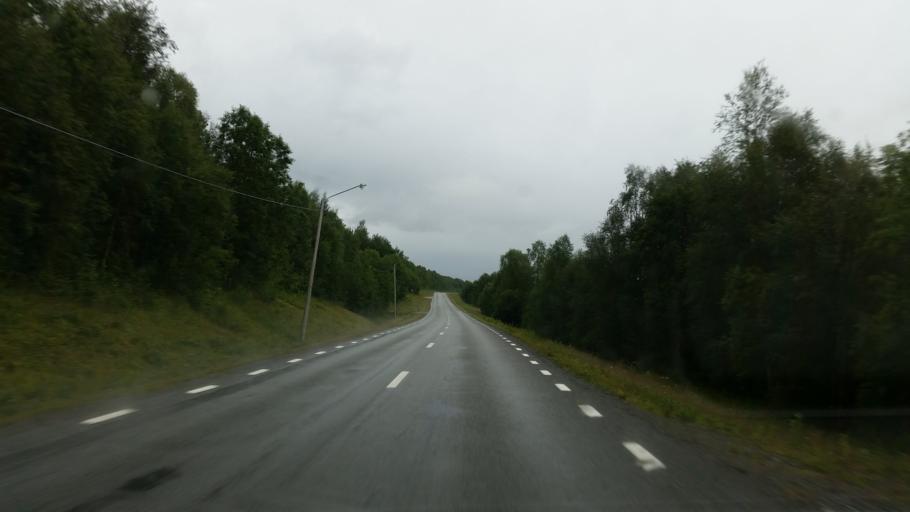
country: NO
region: Nordland
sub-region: Rana
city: Mo i Rana
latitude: 65.8613
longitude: 15.0240
